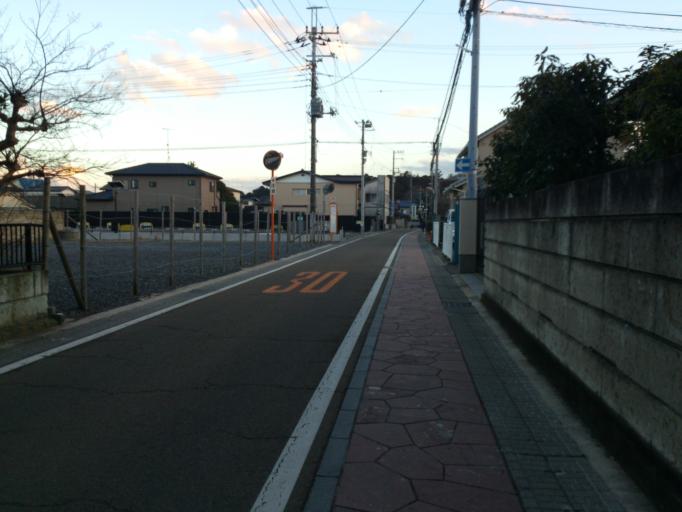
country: JP
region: Ibaraki
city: Mito-shi
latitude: 36.3782
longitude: 140.4531
